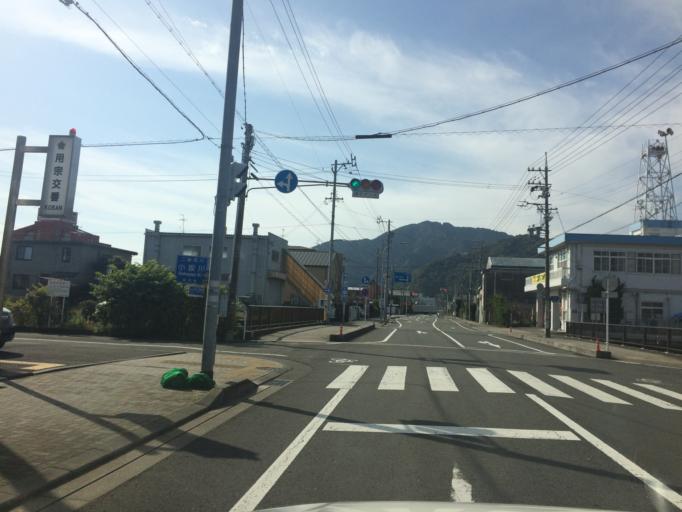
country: JP
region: Shizuoka
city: Shizuoka-shi
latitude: 34.9260
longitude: 138.3662
